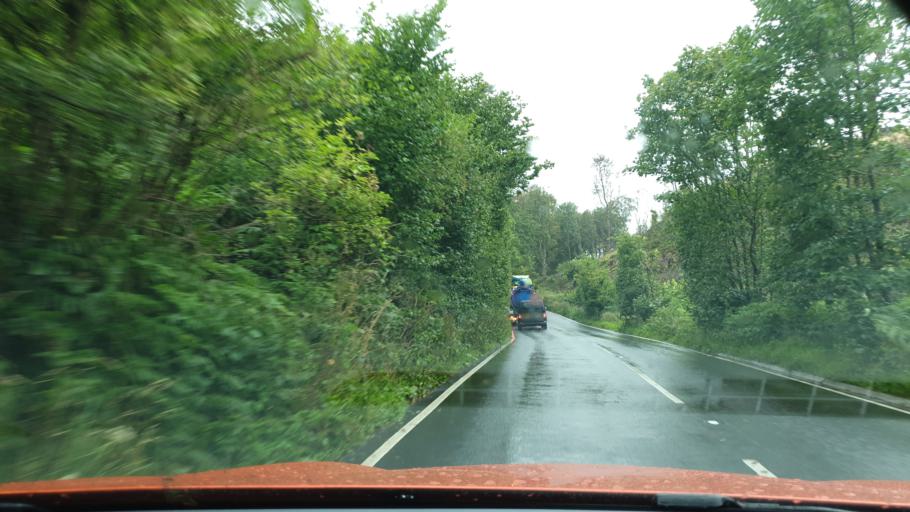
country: GB
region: England
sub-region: Cumbria
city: Askam in Furness
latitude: 54.2638
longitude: -3.1810
